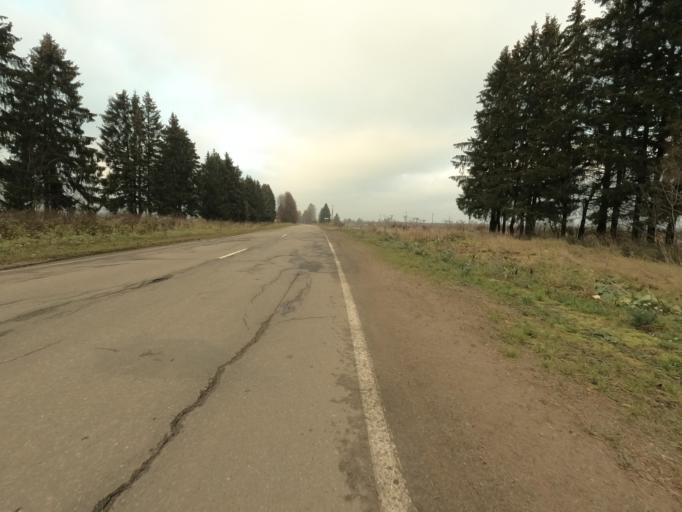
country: RU
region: Leningrad
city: Mga
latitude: 59.7803
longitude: 31.0248
